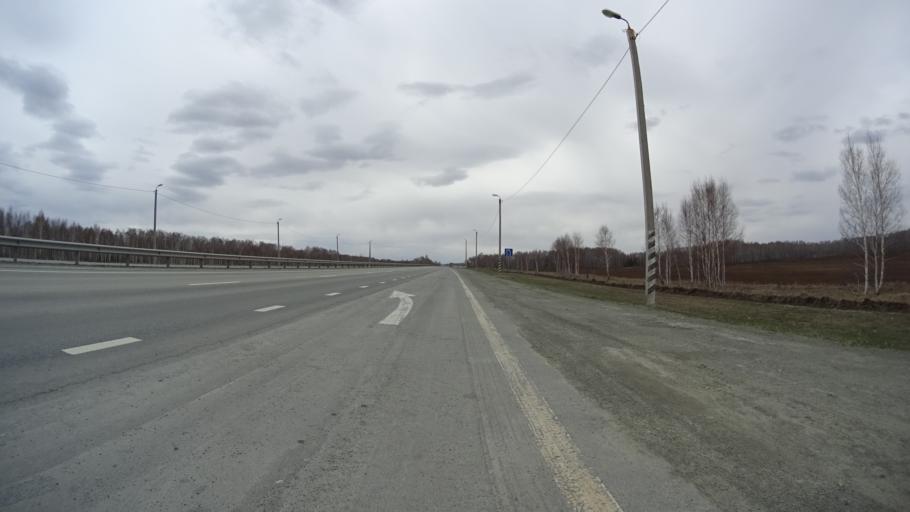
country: RU
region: Chelyabinsk
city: Yemanzhelinka
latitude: 54.8325
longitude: 61.3119
